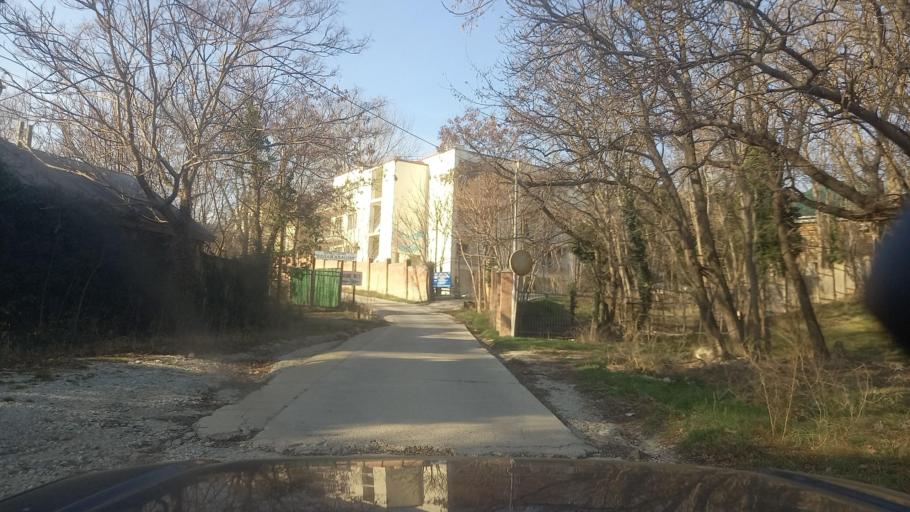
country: RU
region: Krasnodarskiy
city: Myskhako
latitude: 44.6657
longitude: 37.6837
